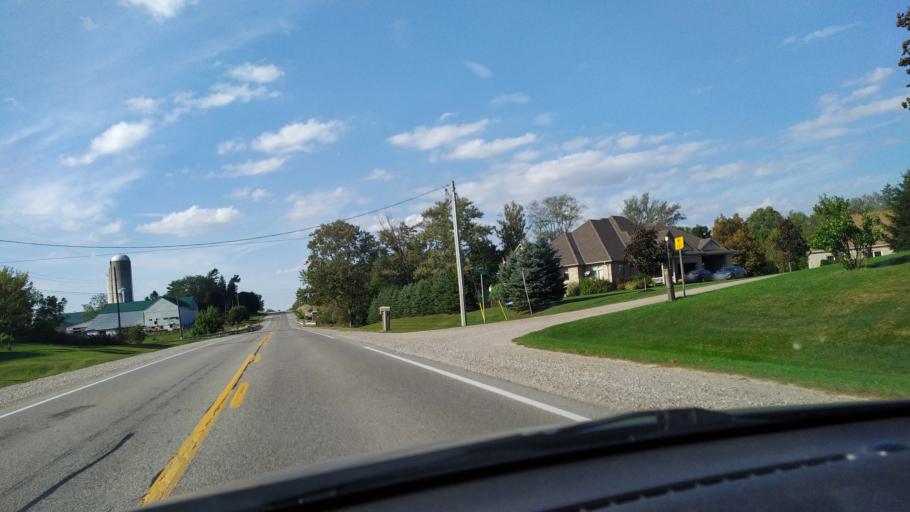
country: CA
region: Ontario
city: Ingersoll
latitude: 43.1642
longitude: -80.9052
